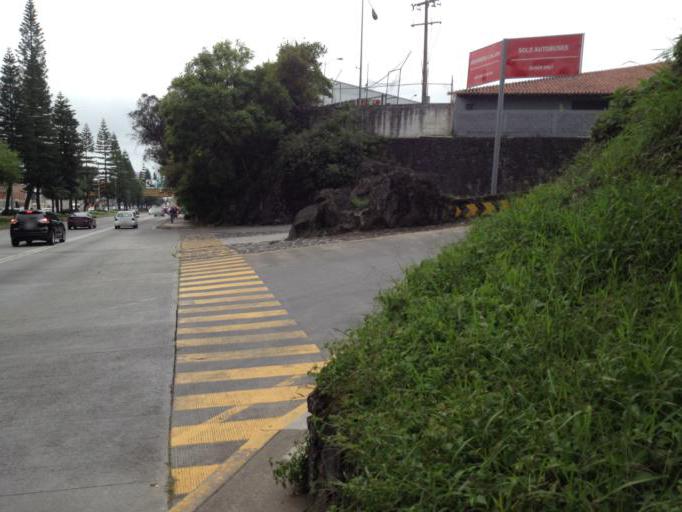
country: MX
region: Veracruz
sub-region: Xalapa
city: Xalapa de Enriquez
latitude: 19.5307
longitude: -96.9026
